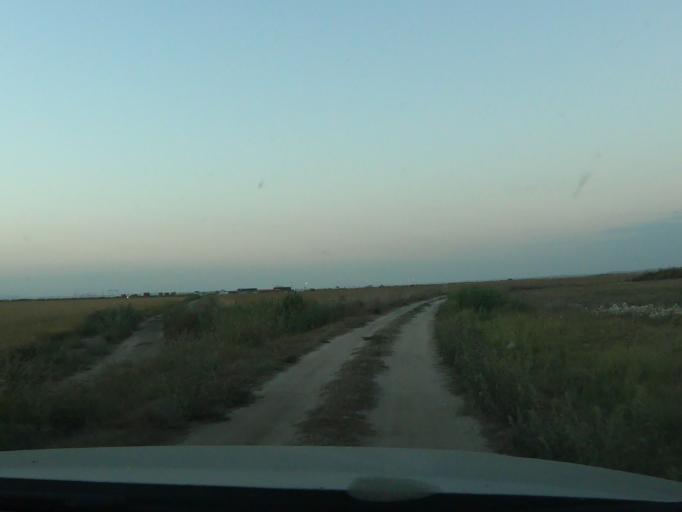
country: PT
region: Setubal
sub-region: Setubal
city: Setubal
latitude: 38.4093
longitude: -8.7562
